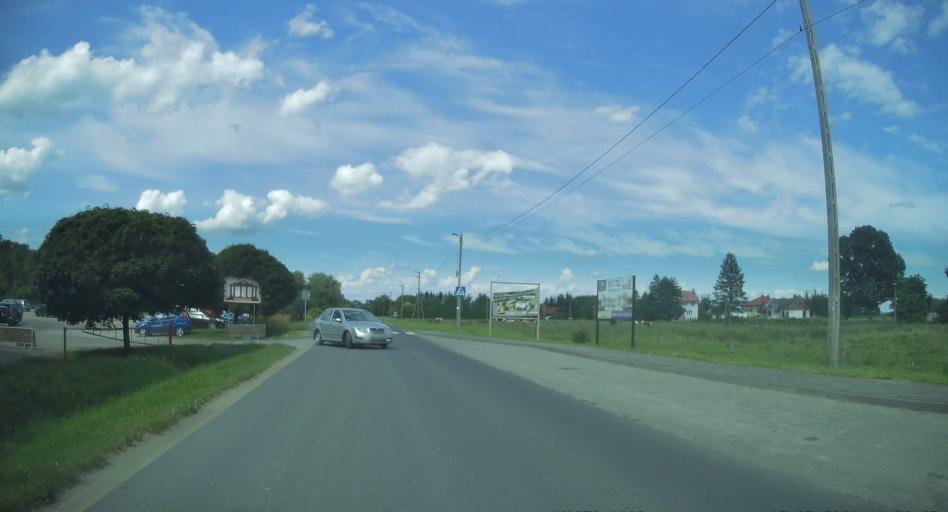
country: PL
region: Subcarpathian Voivodeship
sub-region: Powiat przemyski
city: Medyka
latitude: 49.8174
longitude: 22.8628
